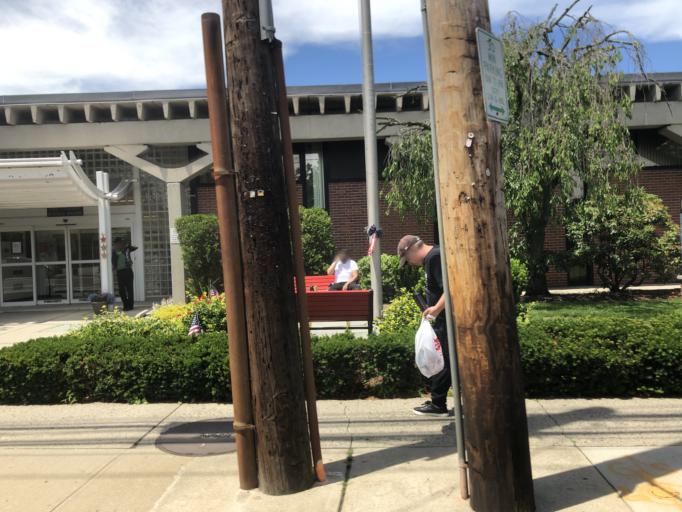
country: US
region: New York
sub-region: Nassau County
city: Uniondale
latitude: 40.7062
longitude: -73.5927
